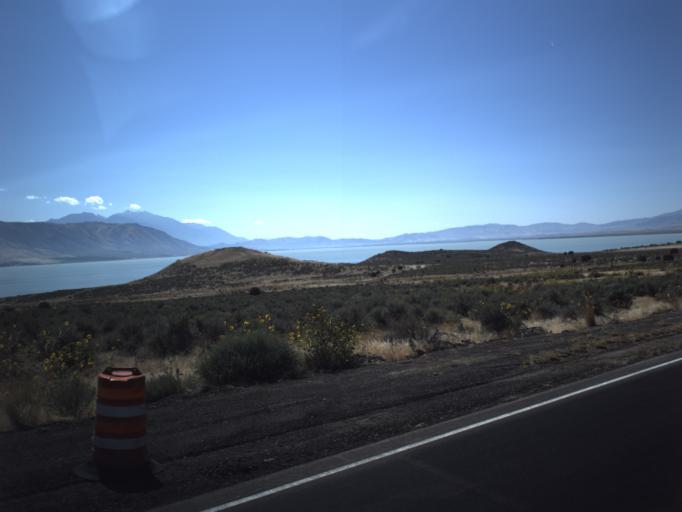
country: US
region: Utah
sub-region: Utah County
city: Saratoga Springs
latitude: 40.2100
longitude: -111.8915
